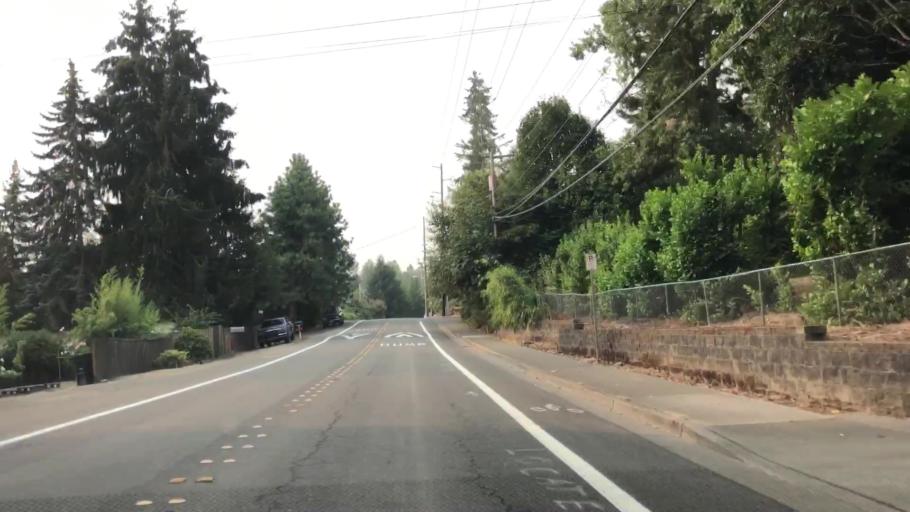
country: US
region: Washington
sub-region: King County
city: Redmond
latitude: 47.6639
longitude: -122.1352
